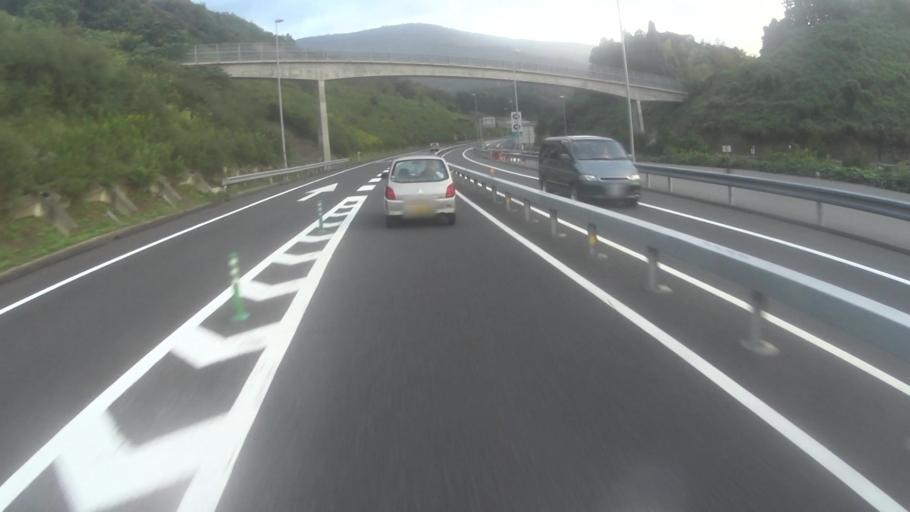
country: JP
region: Kyoto
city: Miyazu
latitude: 35.5139
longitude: 135.1932
